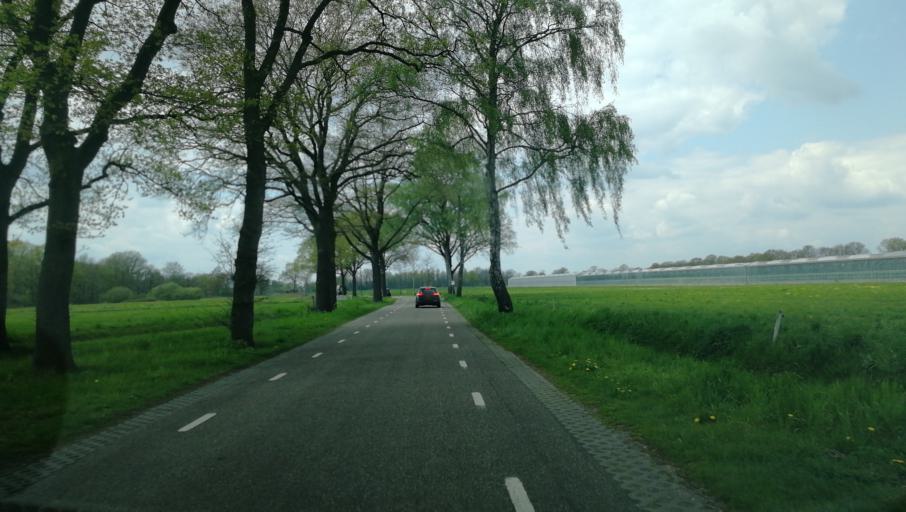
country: NL
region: Limburg
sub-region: Gemeente Peel en Maas
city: Maasbree
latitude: 51.4259
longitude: 6.0239
